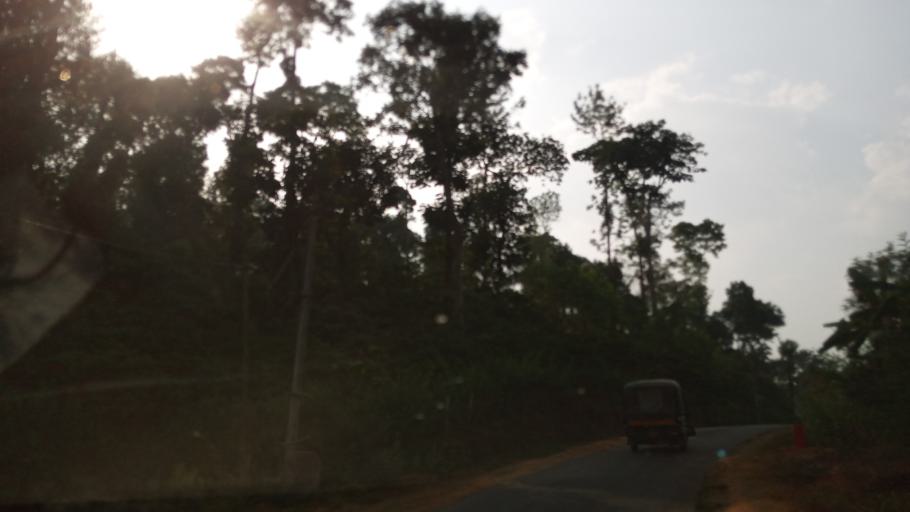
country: IN
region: Karnataka
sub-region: Chikmagalur
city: Mudigere
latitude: 13.0566
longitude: 75.6550
